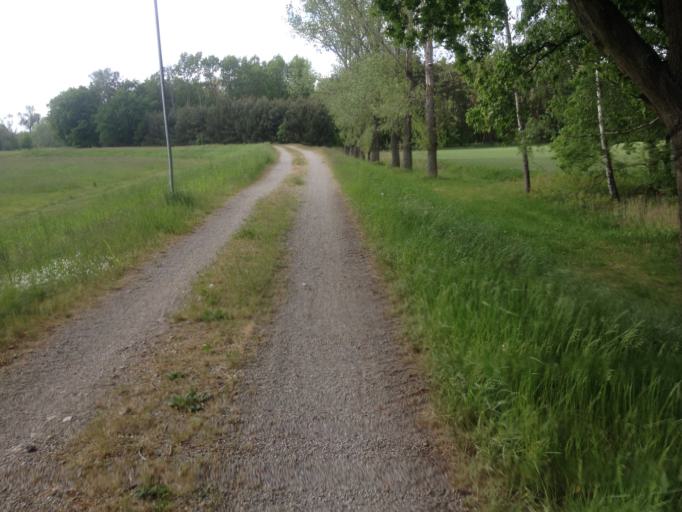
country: DE
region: Brandenburg
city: Drehnow
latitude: 51.8351
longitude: 14.3480
